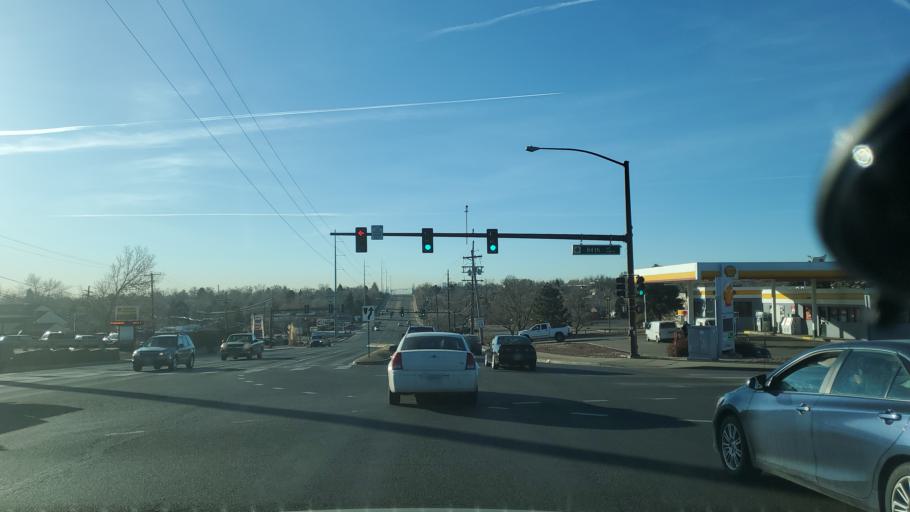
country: US
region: Colorado
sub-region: Adams County
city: Thornton
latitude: 39.8492
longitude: -104.9780
